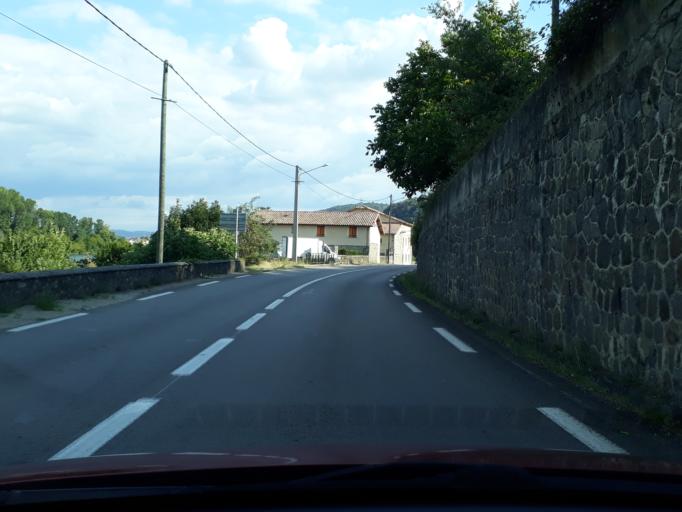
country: FR
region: Rhone-Alpes
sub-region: Departement de l'Ardeche
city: Serrieres
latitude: 45.3254
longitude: 4.7589
